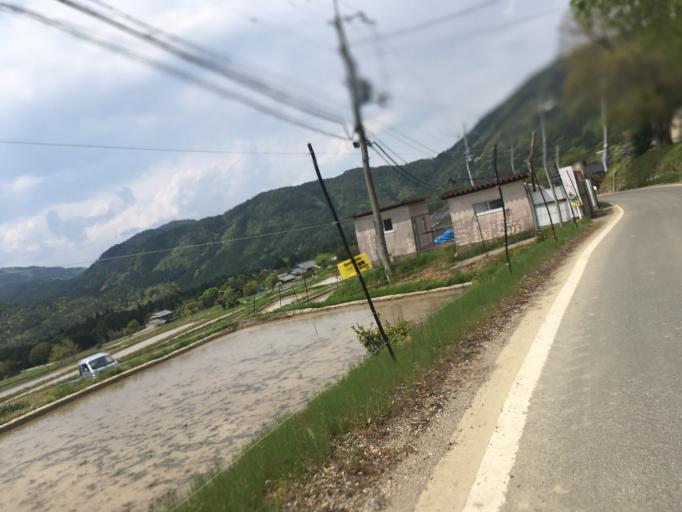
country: JP
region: Kyoto
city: Kameoka
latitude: 35.0829
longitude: 135.6104
